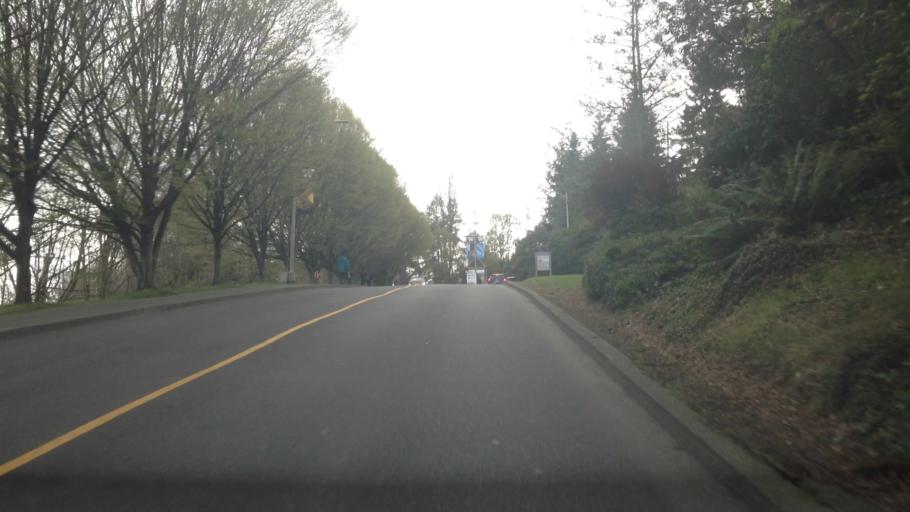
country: US
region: Washington
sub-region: King County
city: Seattle
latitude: 47.6593
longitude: -122.3022
